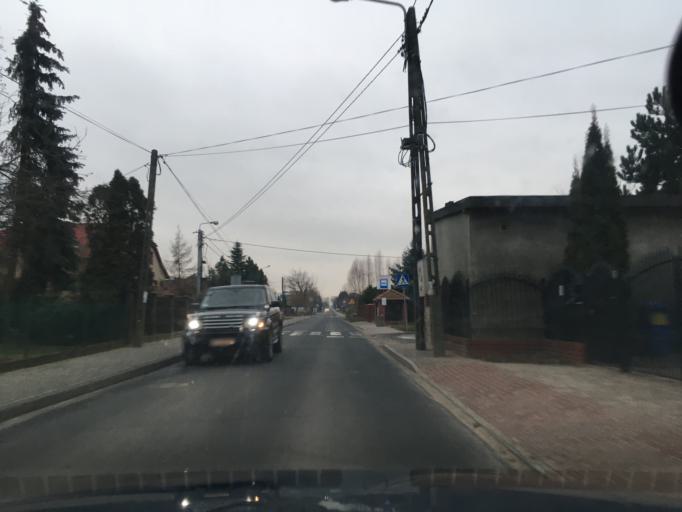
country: PL
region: Masovian Voivodeship
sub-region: Powiat piaseczynski
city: Mysiadlo
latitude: 52.1302
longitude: 20.9799
